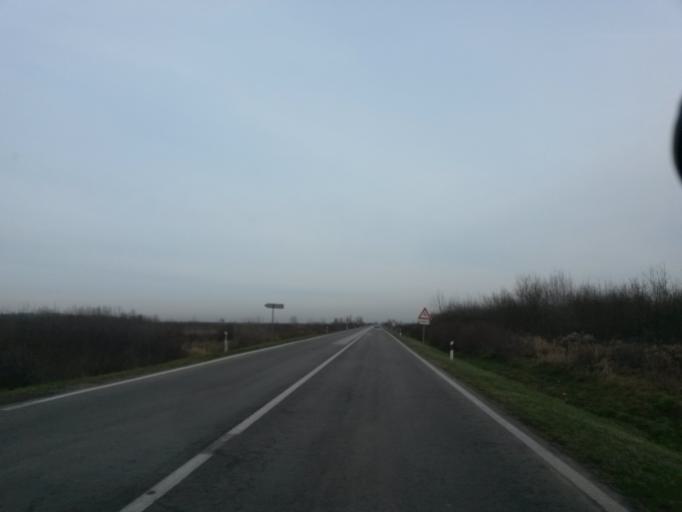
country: HR
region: Vukovarsko-Srijemska
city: Nustar
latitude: 45.3418
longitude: 18.8768
